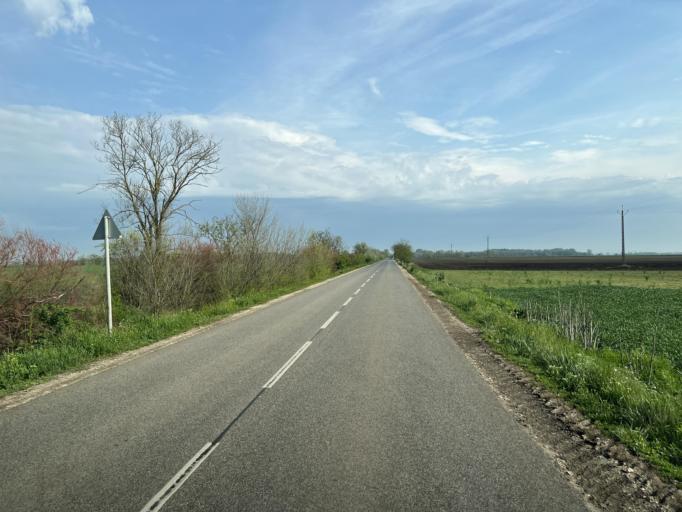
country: HU
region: Pest
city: Cegled
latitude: 47.2383
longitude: 19.7774
